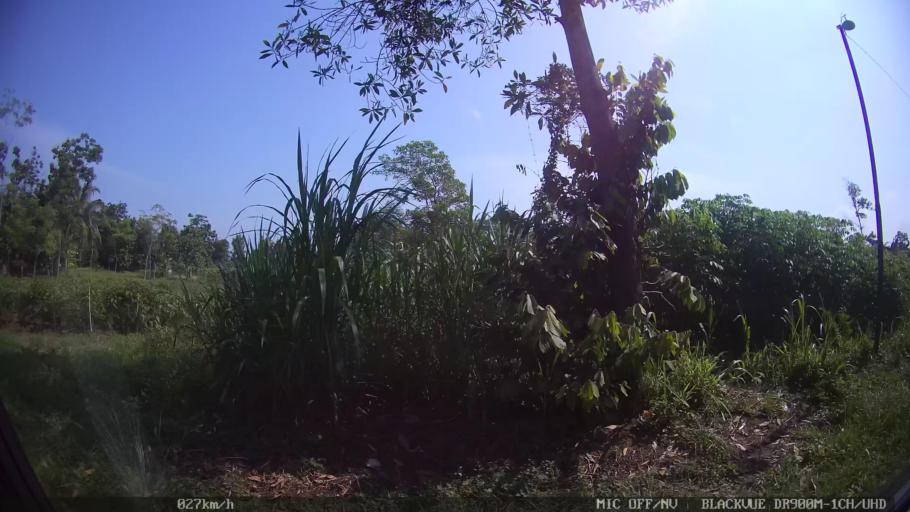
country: ID
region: Lampung
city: Natar
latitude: -5.2539
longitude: 105.1925
